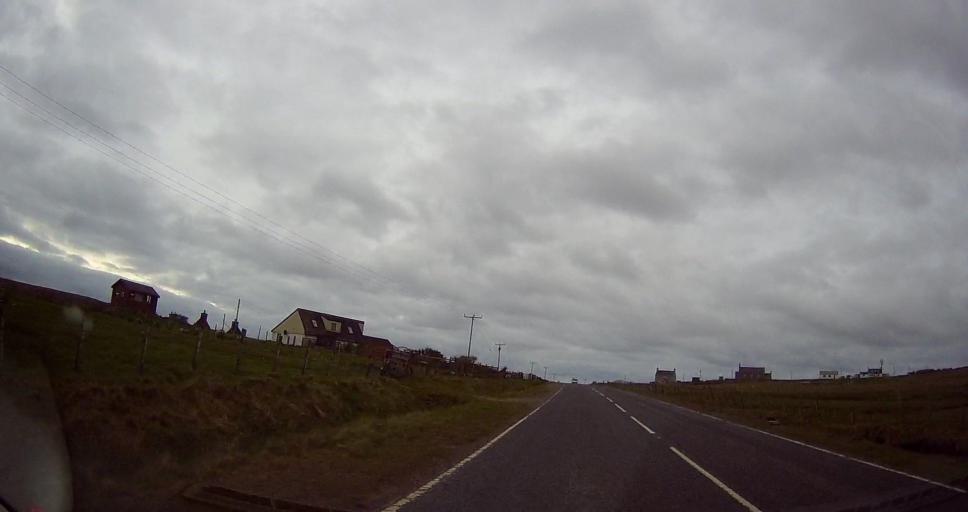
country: GB
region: Scotland
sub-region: Shetland Islands
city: Shetland
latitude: 60.6633
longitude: -1.0536
